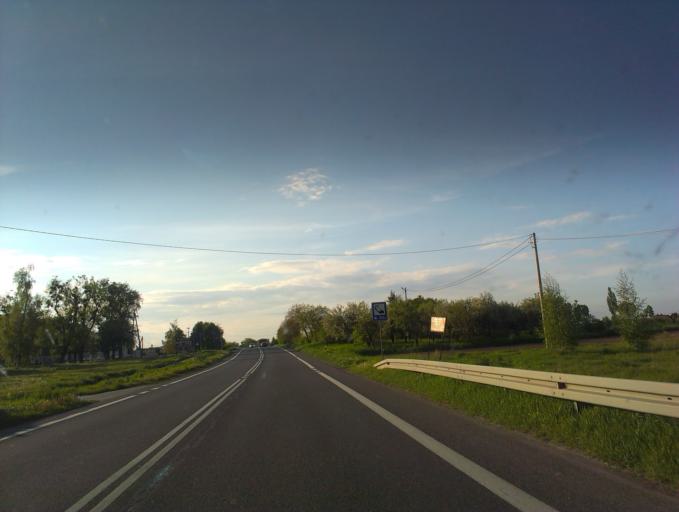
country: PL
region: Swietokrzyskie
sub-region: Powiat opatowski
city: Sadowie
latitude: 50.8626
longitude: 21.3748
